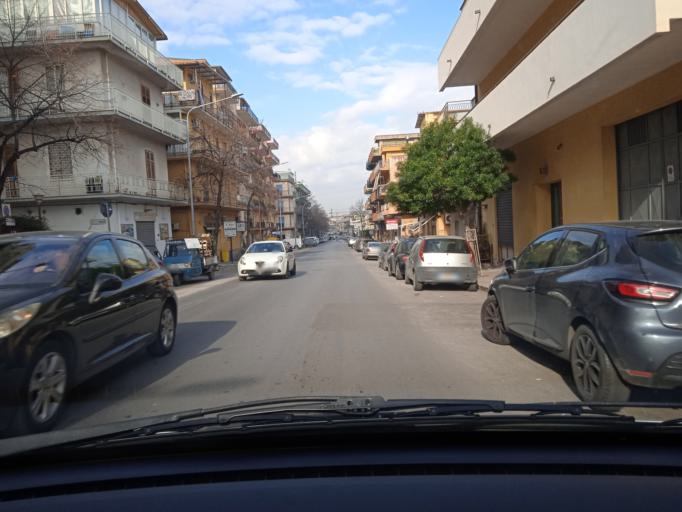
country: IT
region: Sicily
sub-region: Palermo
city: Villabate
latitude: 38.0786
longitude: 13.4451
